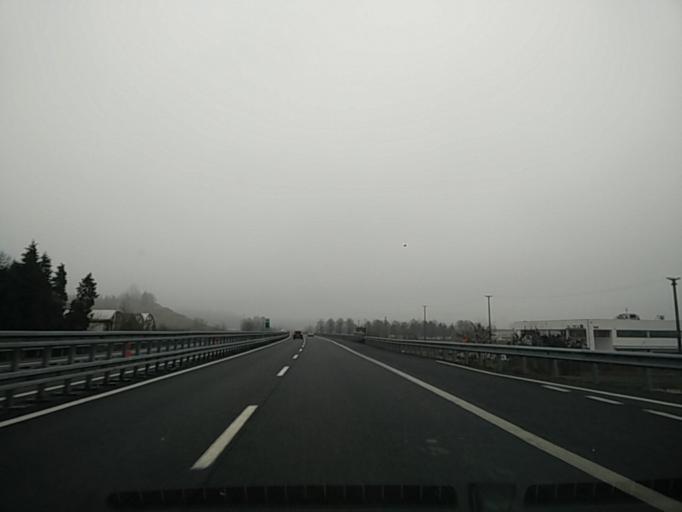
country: IT
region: Piedmont
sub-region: Provincia di Asti
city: Azzano d'Asti
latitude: 44.9082
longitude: 8.2621
